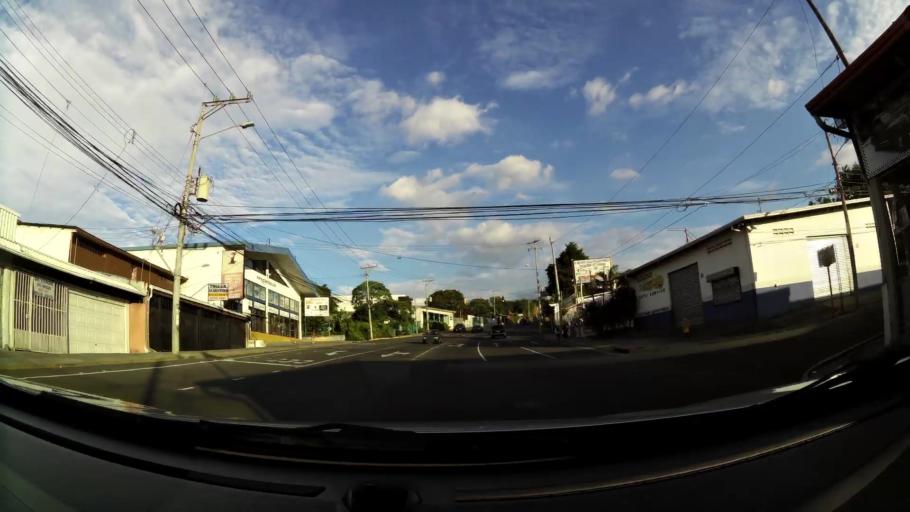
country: CR
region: Heredia
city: Llorente
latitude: 10.0001
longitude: -84.1475
